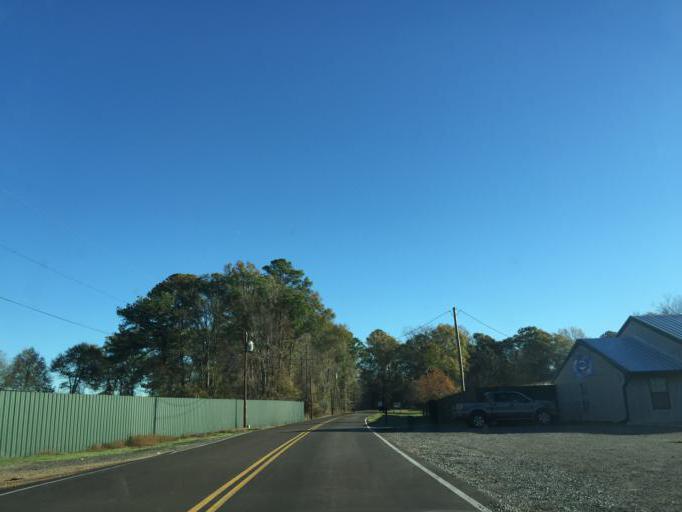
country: US
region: Mississippi
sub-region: Hinds County
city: Jackson
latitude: 32.2842
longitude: -90.1613
